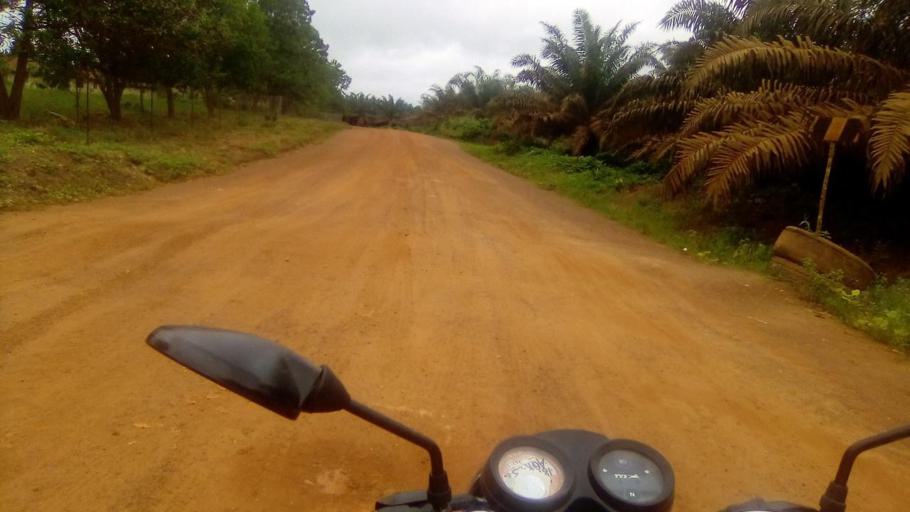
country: SL
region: Southern Province
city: Tongole
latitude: 7.4329
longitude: -11.8582
